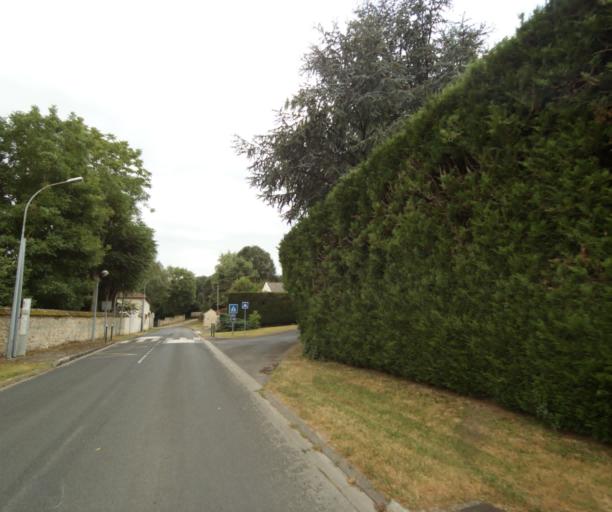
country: FR
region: Ile-de-France
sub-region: Departement de Seine-et-Marne
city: Cely
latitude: 48.4657
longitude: 2.5208
